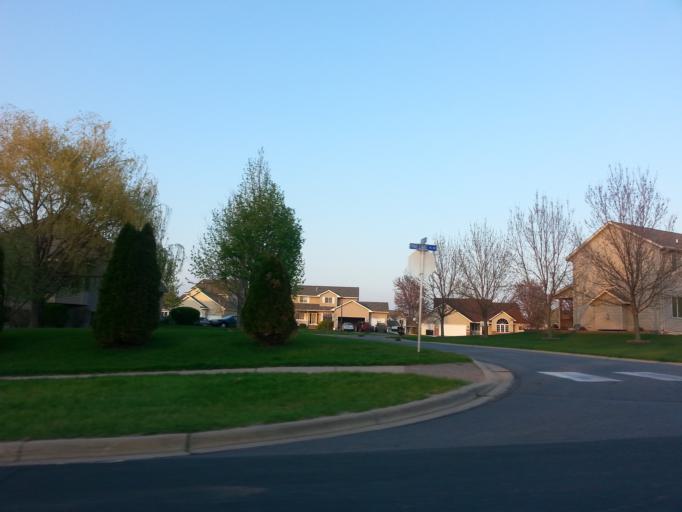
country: US
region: Minnesota
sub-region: Scott County
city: Prior Lake
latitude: 44.7410
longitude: -93.4292
